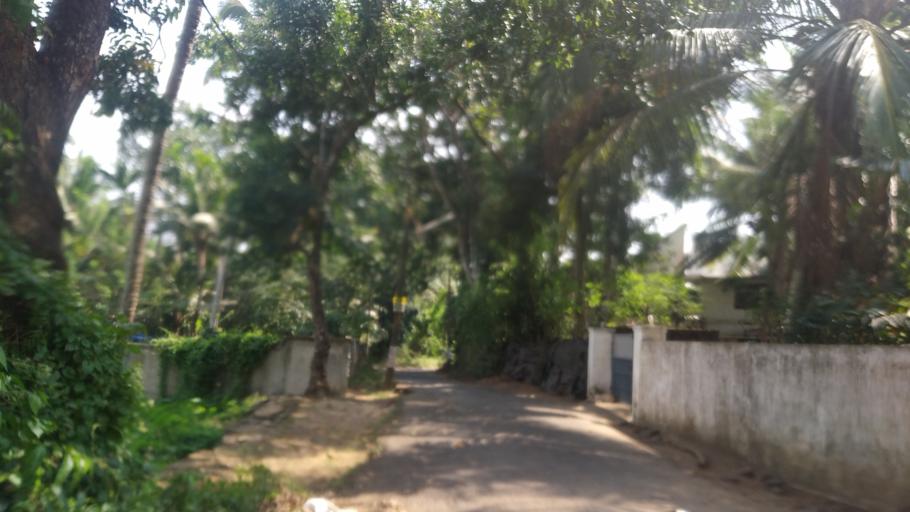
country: IN
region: Kerala
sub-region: Ernakulam
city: Elur
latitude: 10.1273
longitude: 76.2330
